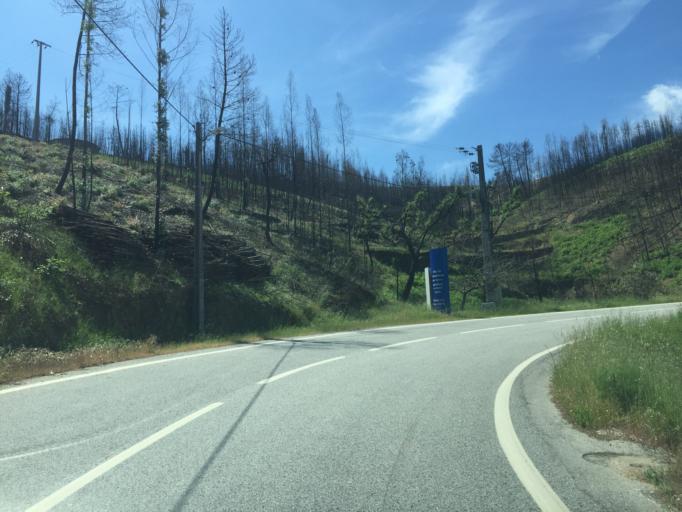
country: PT
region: Coimbra
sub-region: Pampilhosa da Serra
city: Pampilhosa da Serra
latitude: 40.0411
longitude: -7.9547
